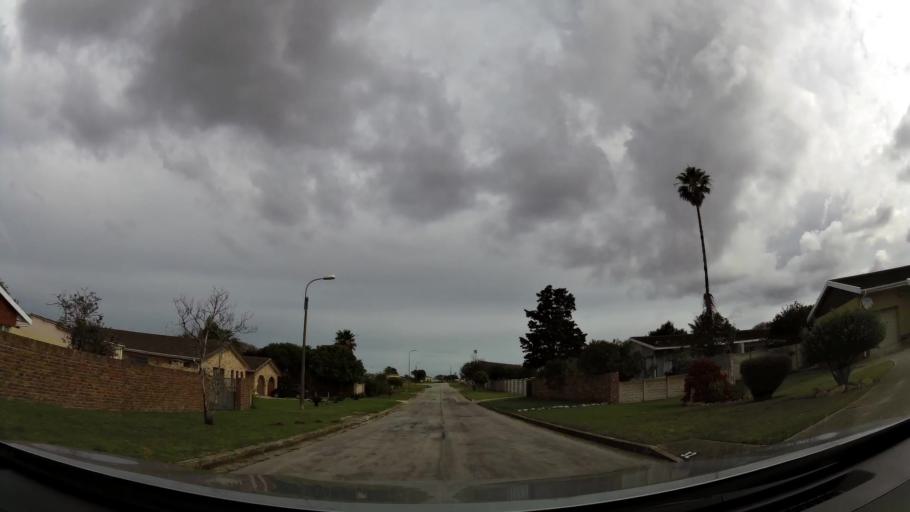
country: ZA
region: Eastern Cape
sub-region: Nelson Mandela Bay Metropolitan Municipality
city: Port Elizabeth
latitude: -33.9362
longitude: 25.5106
